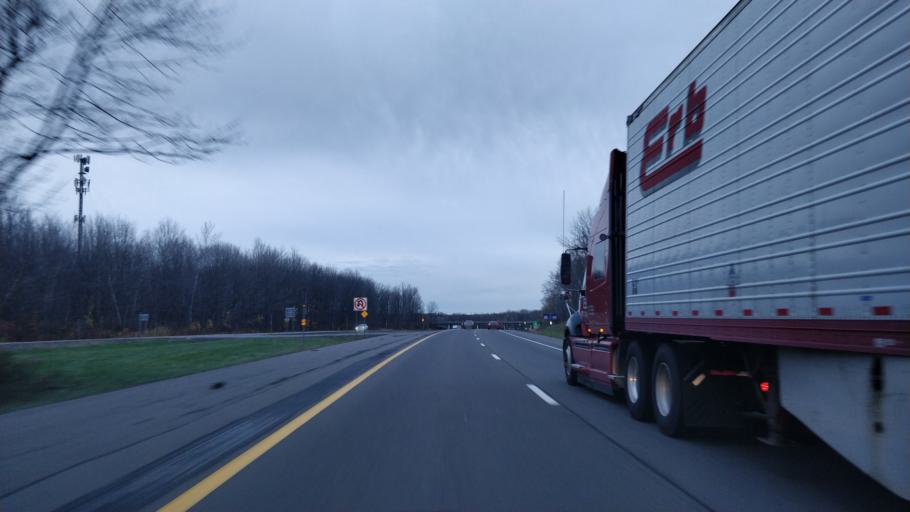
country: US
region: New York
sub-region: Oswego County
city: Central Square
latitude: 43.4002
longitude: -76.1181
